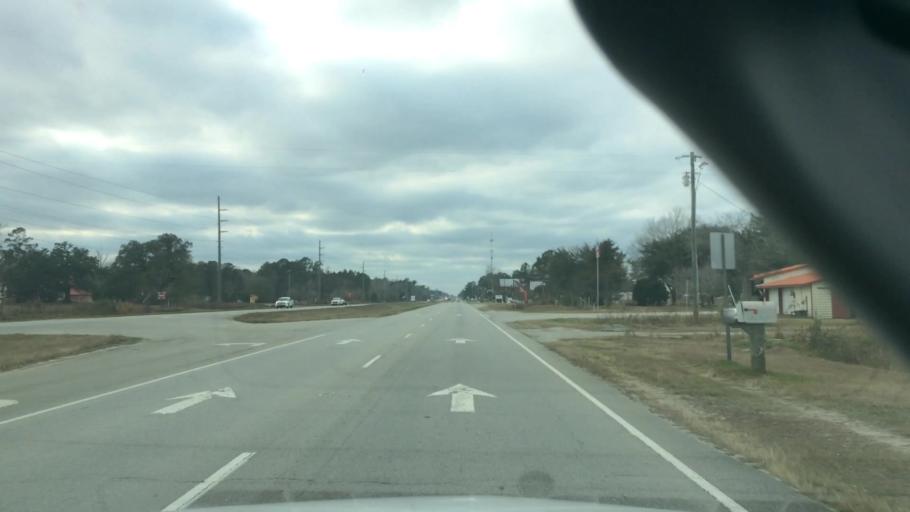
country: US
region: North Carolina
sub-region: Brunswick County
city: Sunset Beach
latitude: 33.9500
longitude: -78.4791
